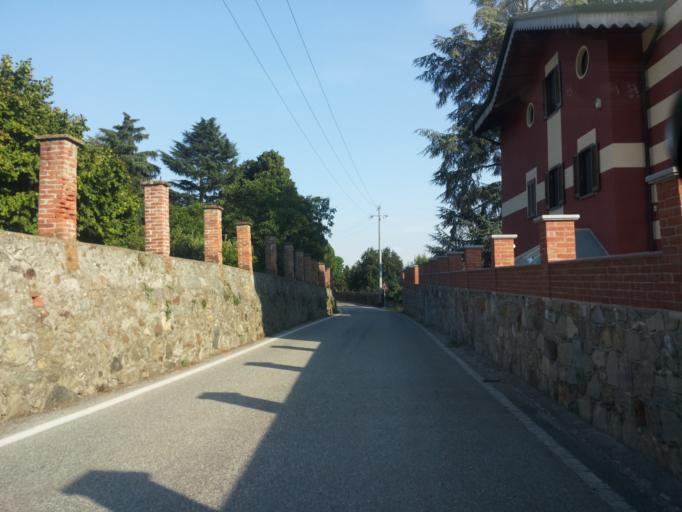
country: IT
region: Piedmont
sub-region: Provincia di Torino
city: Piverone
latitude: 45.4516
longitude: 7.9999
